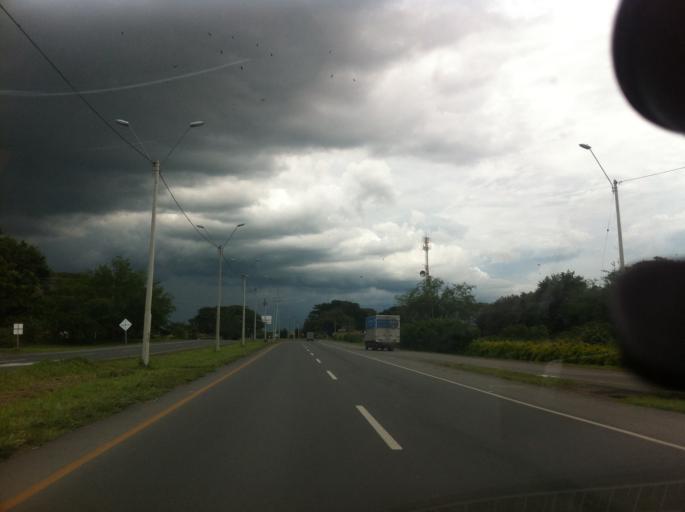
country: CO
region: Valle del Cauca
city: El Cerrito
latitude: 3.7014
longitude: -76.3187
